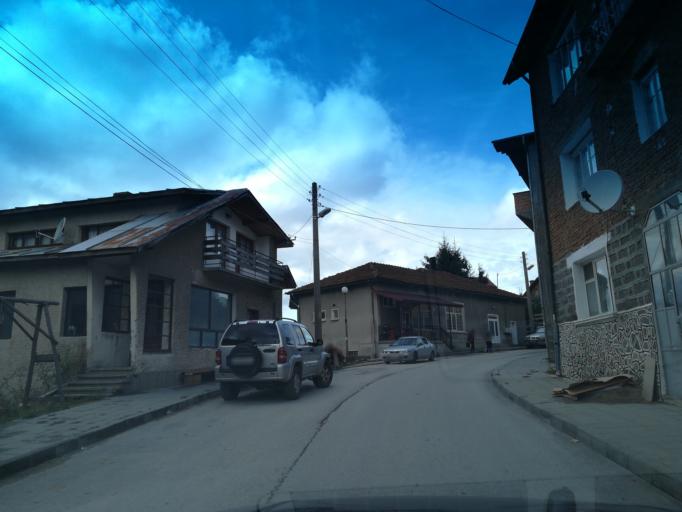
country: BG
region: Pazardzhik
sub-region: Obshtina Batak
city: Batak
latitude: 41.9364
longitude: 24.2712
